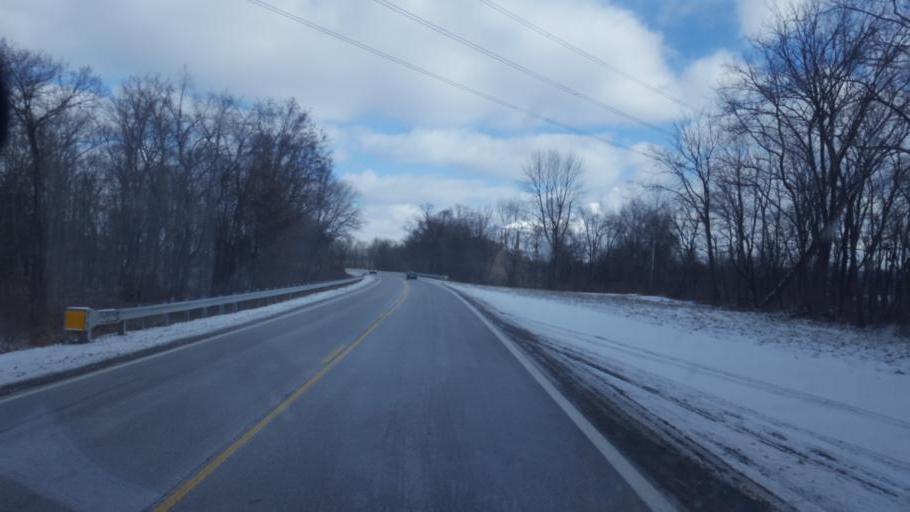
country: US
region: Ohio
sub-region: Muskingum County
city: Dresden
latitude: 40.1697
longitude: -81.9124
